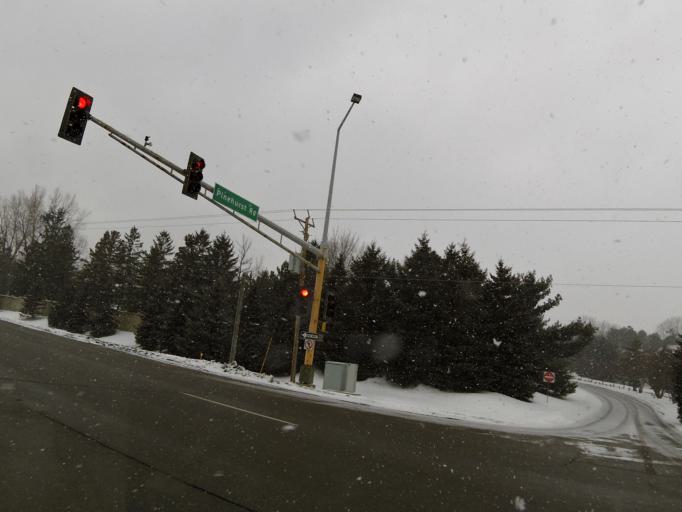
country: US
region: Minnesota
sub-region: Washington County
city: Woodbury
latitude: 44.9294
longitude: -92.9342
